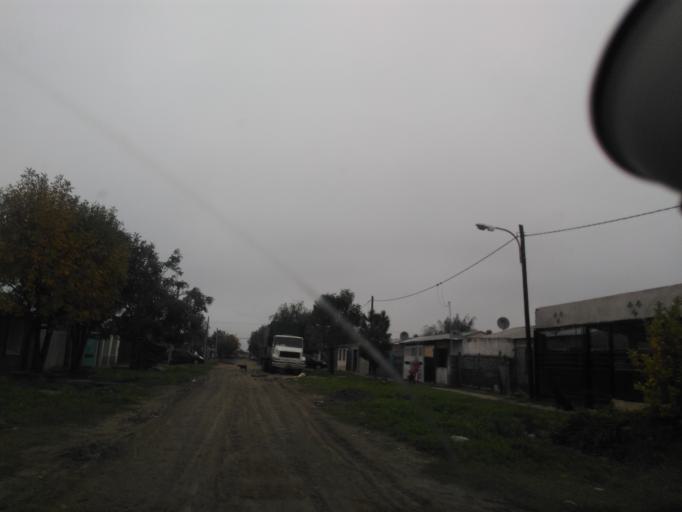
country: AR
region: Chaco
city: Fontana
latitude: -27.3999
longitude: -58.9934
